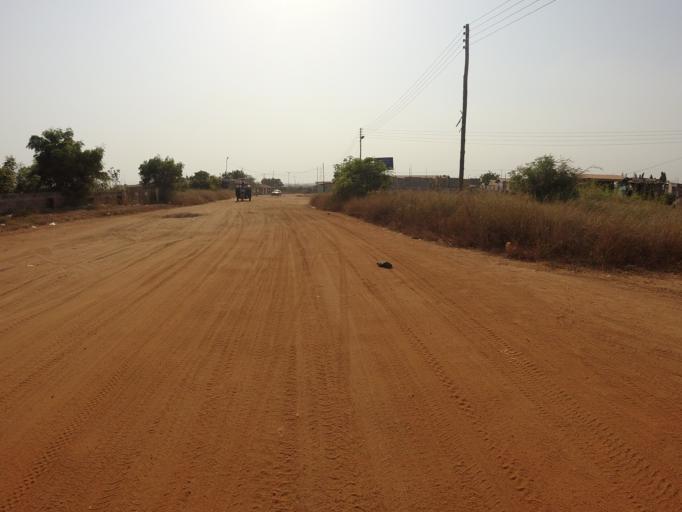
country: GH
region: Greater Accra
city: Tema
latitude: 5.7055
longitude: 0.0586
